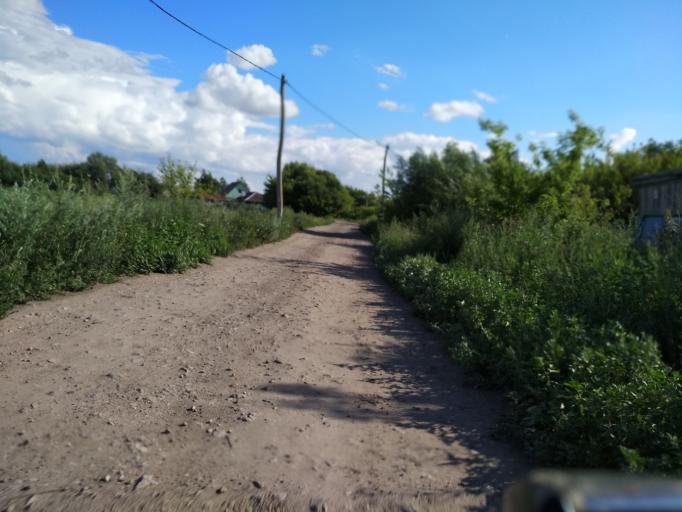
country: RU
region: Lipetsk
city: Dobrinka
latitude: 52.0322
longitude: 40.5629
